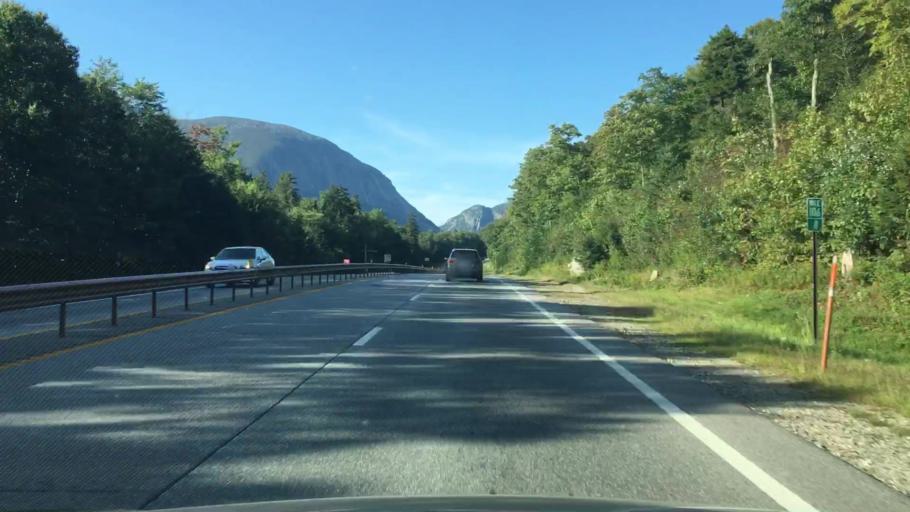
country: US
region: New Hampshire
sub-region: Grafton County
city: Deerfield
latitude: 44.1234
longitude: -71.6818
